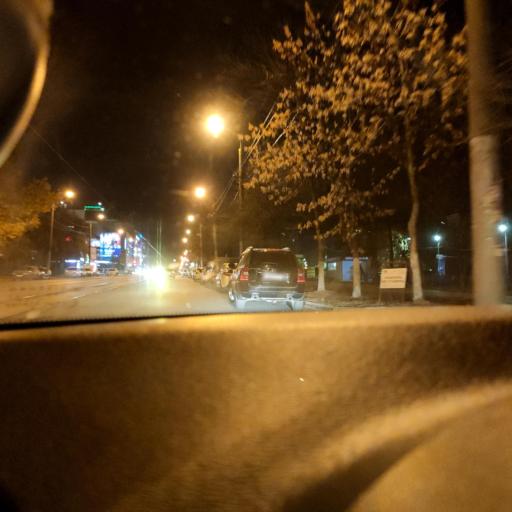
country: RU
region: Samara
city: Samara
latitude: 53.1918
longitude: 50.1942
